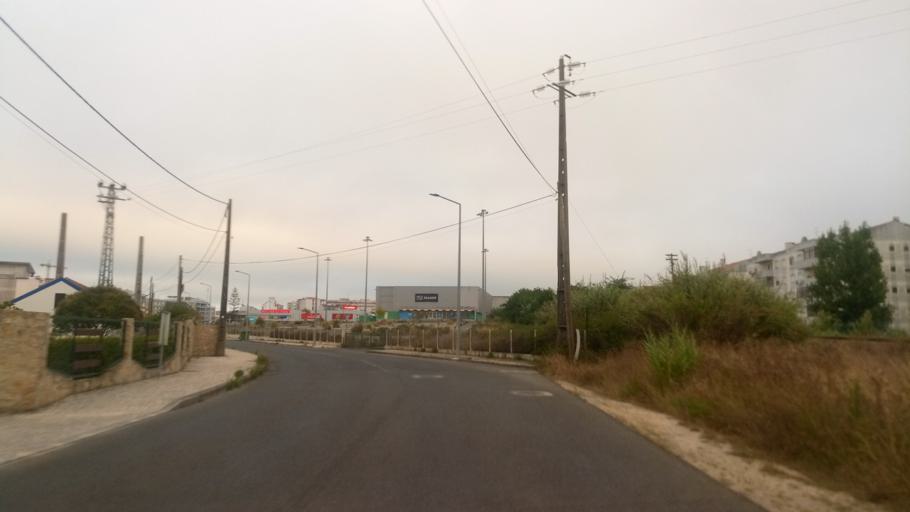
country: PT
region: Leiria
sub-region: Caldas da Rainha
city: Caldas da Rainha
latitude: 39.4165
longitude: -9.1424
